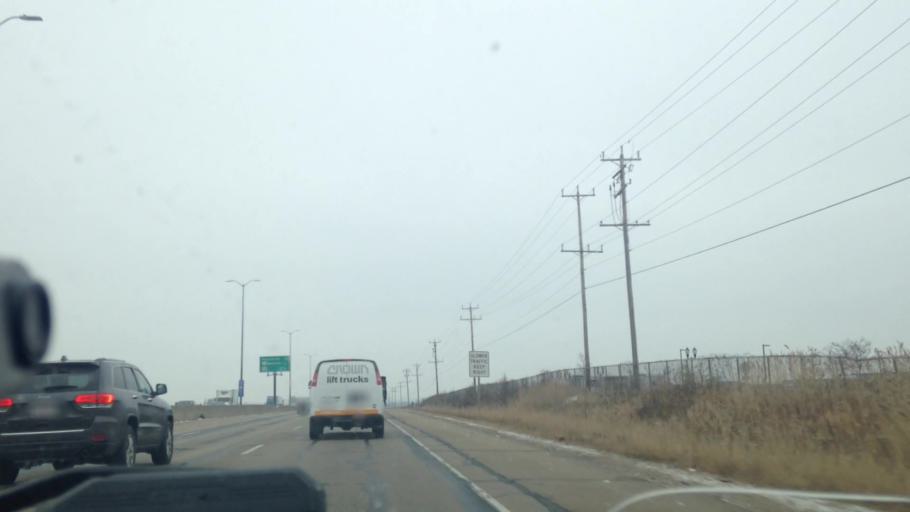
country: US
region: Wisconsin
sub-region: Waukesha County
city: Menomonee Falls
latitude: 43.1873
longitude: -88.1126
